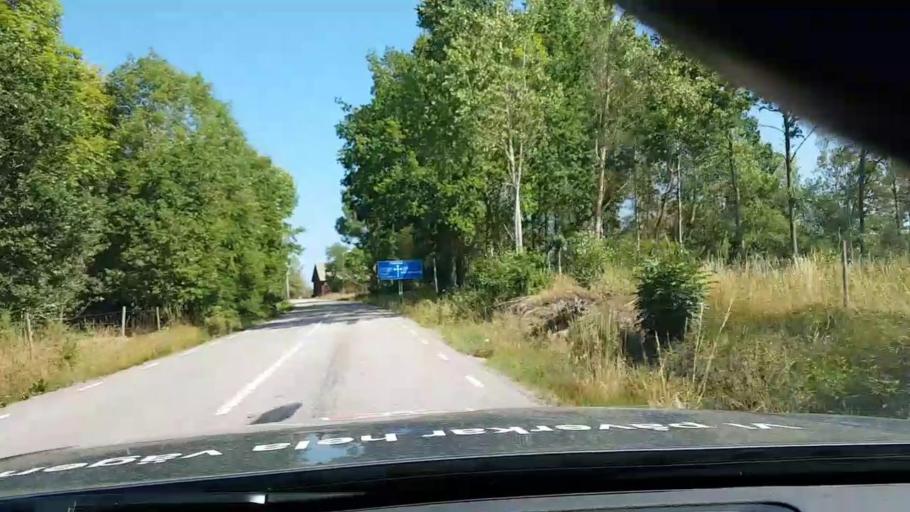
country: SE
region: Kalmar
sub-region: Hultsfreds Kommun
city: Virserum
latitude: 57.1340
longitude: 15.6592
